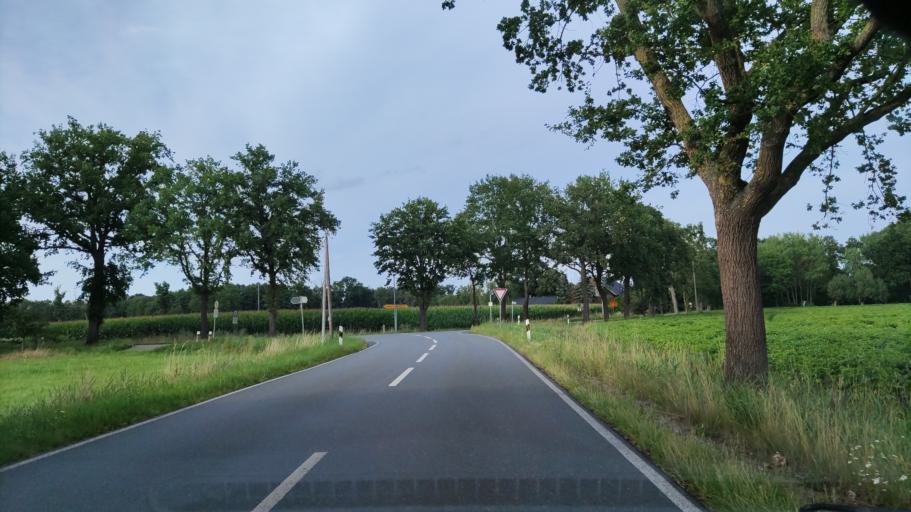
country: DE
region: Lower Saxony
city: Jameln
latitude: 53.0535
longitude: 11.1374
